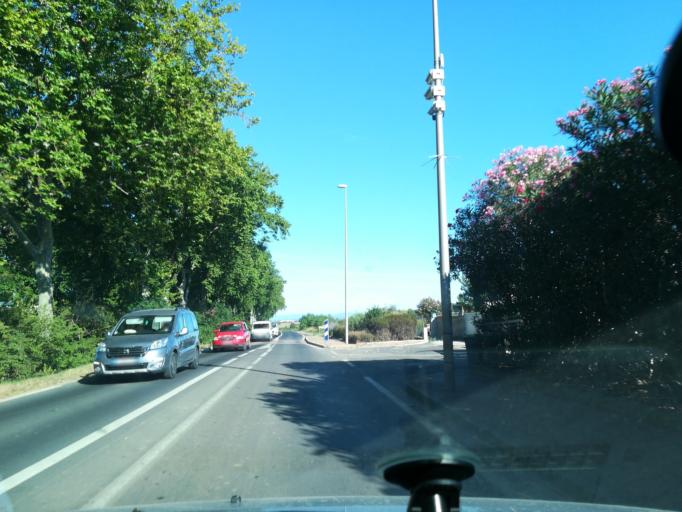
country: FR
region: Languedoc-Roussillon
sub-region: Departement de l'Herault
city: Portiragnes
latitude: 43.3073
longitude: 3.3259
